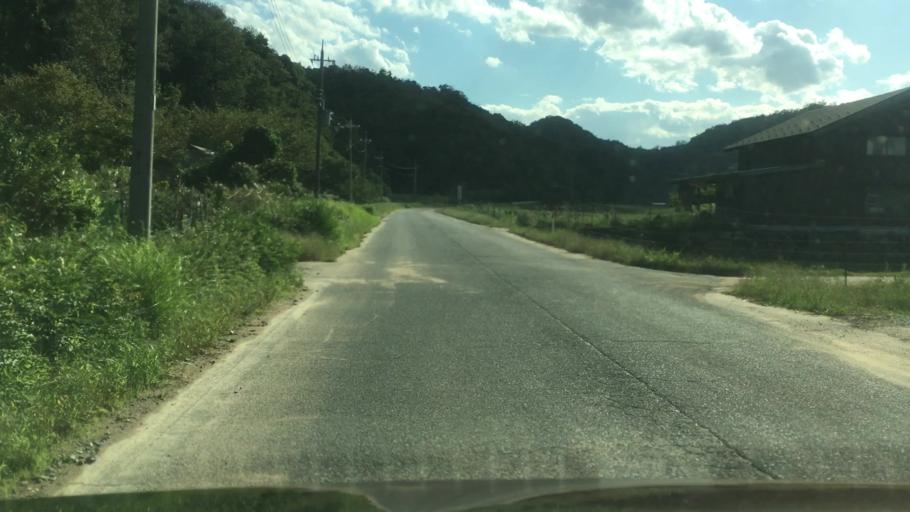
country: JP
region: Hyogo
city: Toyooka
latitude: 35.6480
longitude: 134.9650
